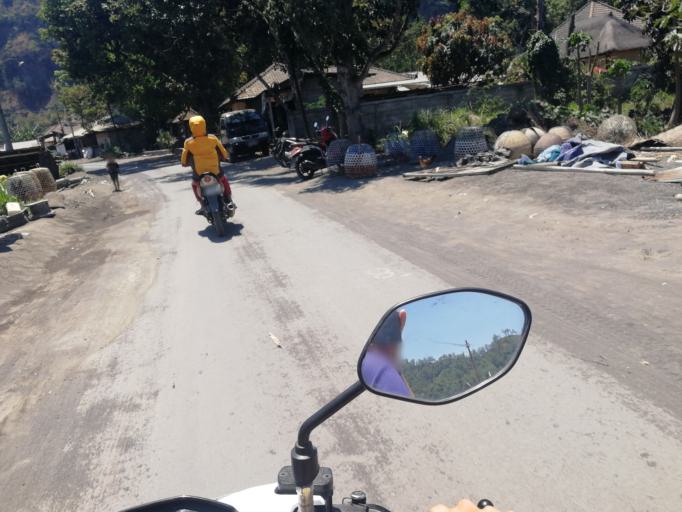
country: ID
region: Bali
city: Banjar Trunyan
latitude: -8.2232
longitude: 115.4112
